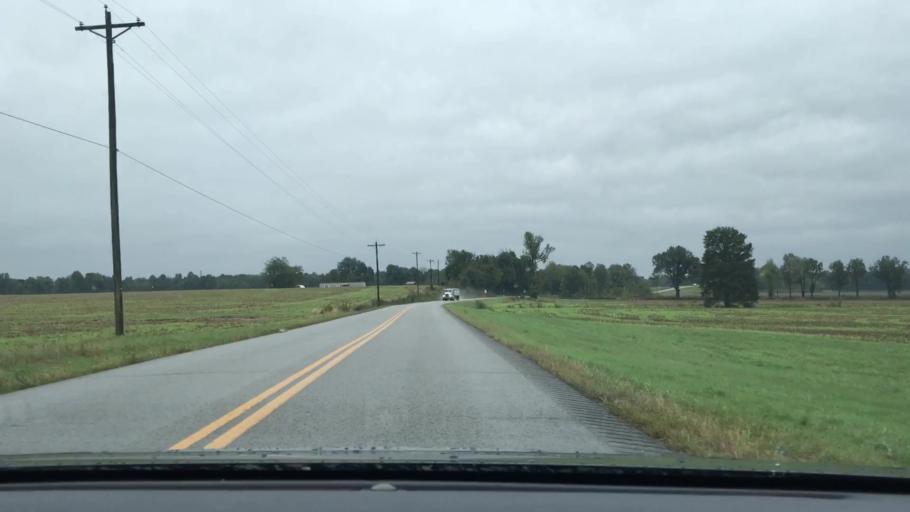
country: US
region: Kentucky
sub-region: McLean County
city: Calhoun
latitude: 37.4686
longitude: -87.2331
